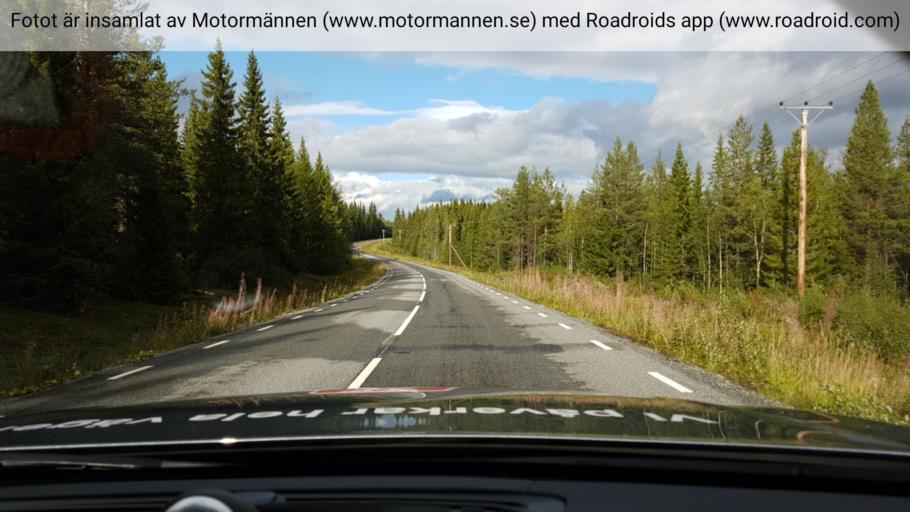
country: SE
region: Jaemtland
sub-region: Krokoms Kommun
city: Krokom
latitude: 63.6556
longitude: 14.4742
